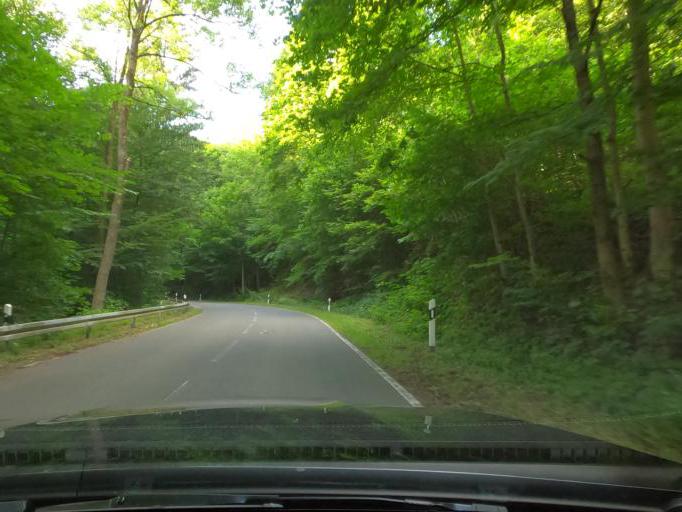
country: DE
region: Lower Saxony
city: Clausthal-Zellerfeld
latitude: 51.7616
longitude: 10.3167
